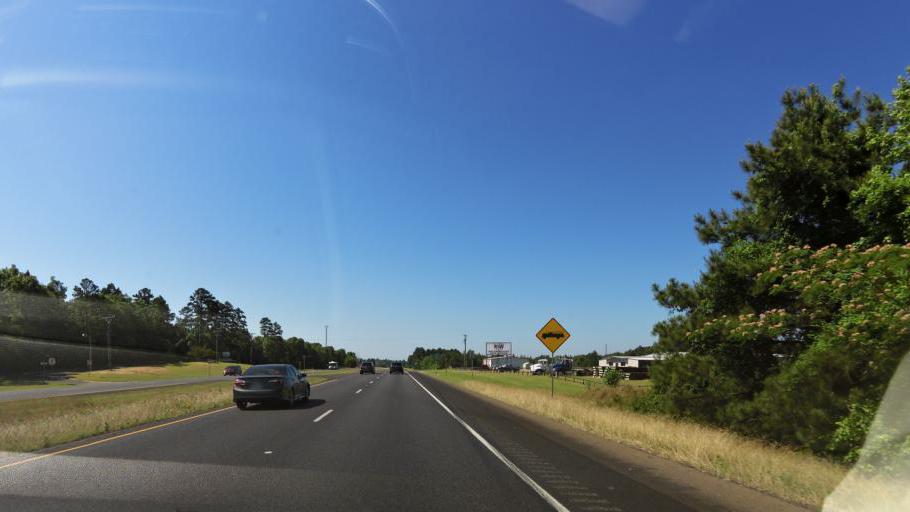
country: US
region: Texas
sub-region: Nacogdoches County
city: Nacogdoches
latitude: 31.5345
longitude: -94.6940
